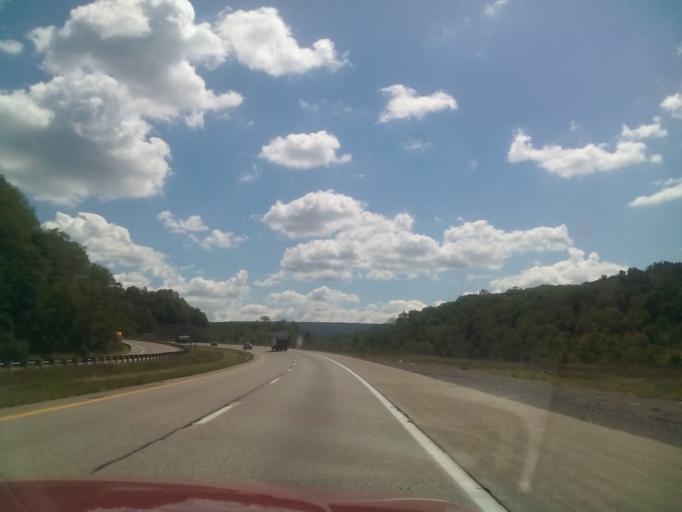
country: US
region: Pennsylvania
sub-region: Luzerne County
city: Nescopeck
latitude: 41.0071
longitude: -76.1654
